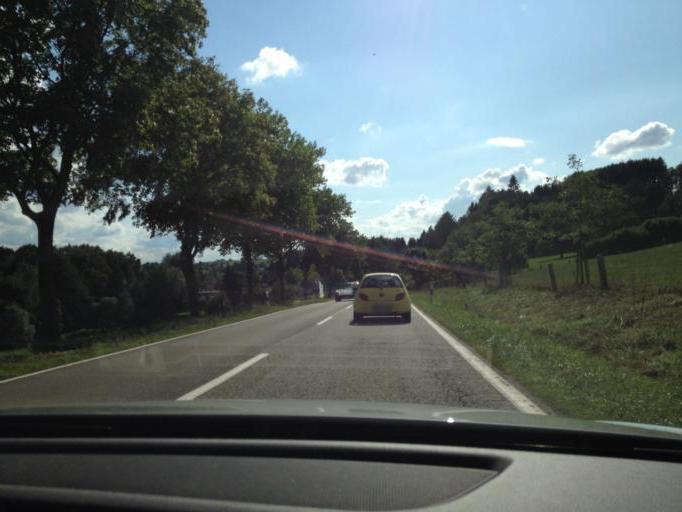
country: DE
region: Saarland
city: Illingen
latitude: 49.3948
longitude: 7.0772
